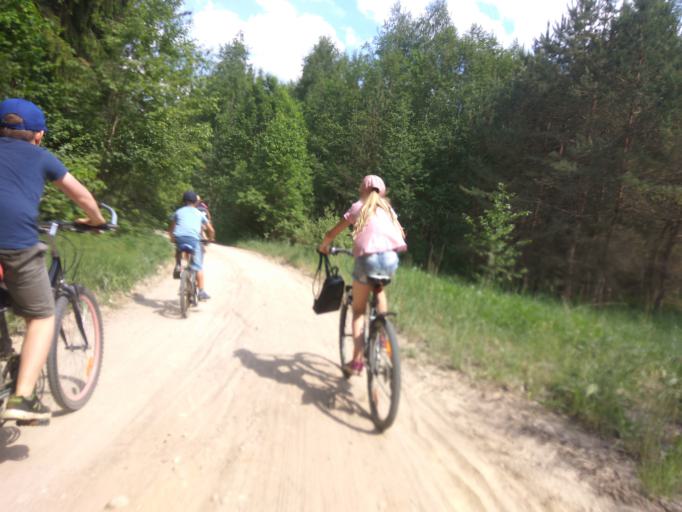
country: LV
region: Kuldigas Rajons
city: Kuldiga
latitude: 56.9034
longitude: 21.9261
